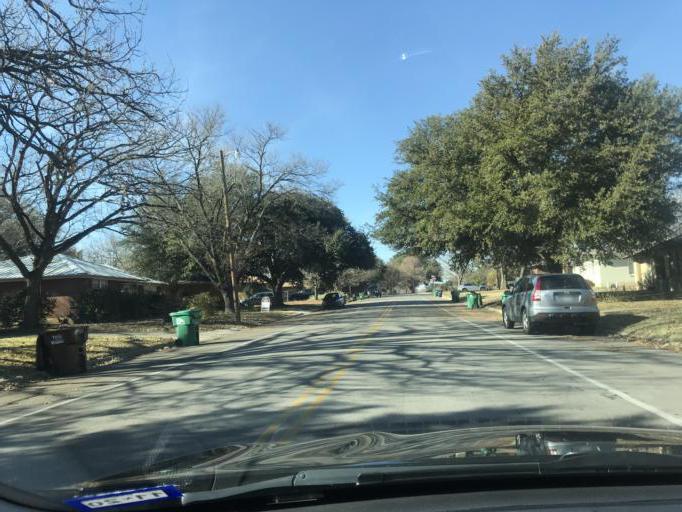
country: US
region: Texas
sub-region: Denton County
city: Denton
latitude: 33.2234
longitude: -97.1485
